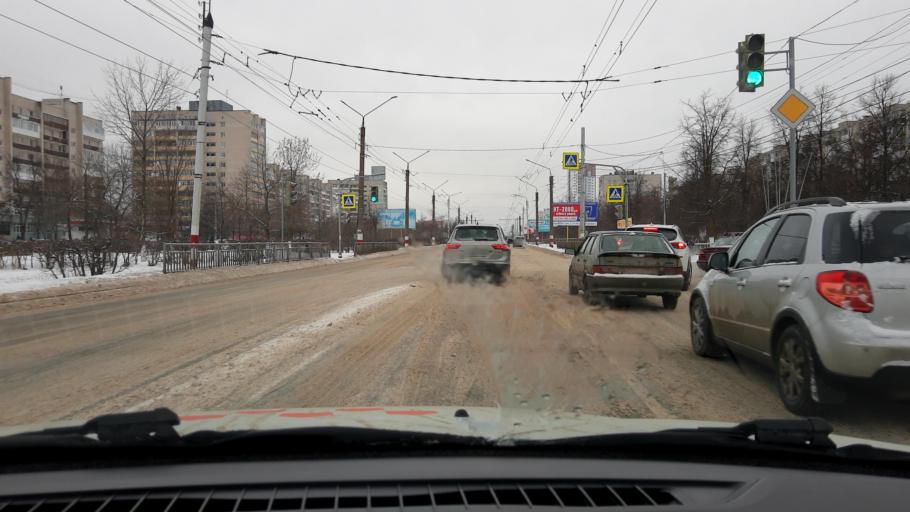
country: RU
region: Nizjnij Novgorod
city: Dzerzhinsk
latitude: 56.2269
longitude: 43.3985
